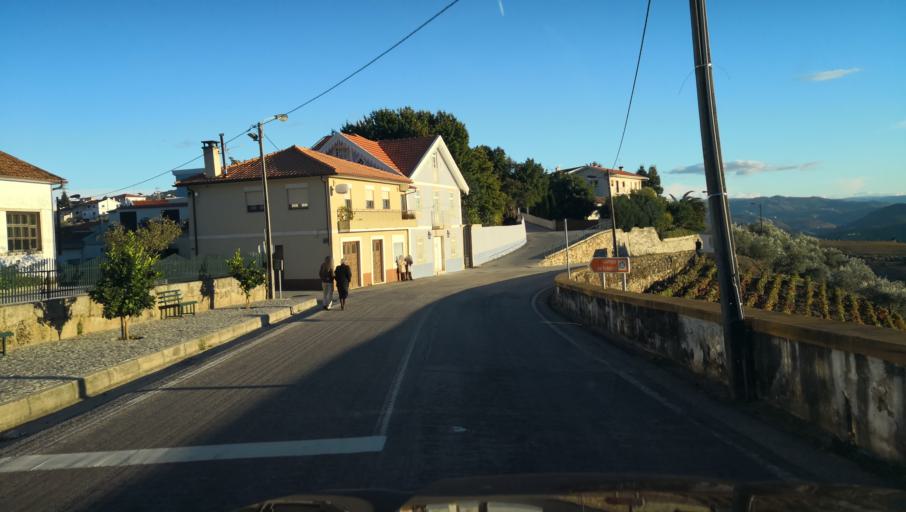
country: PT
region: Vila Real
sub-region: Santa Marta de Penaguiao
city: Santa Marta de Penaguiao
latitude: 41.2516
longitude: -7.7714
